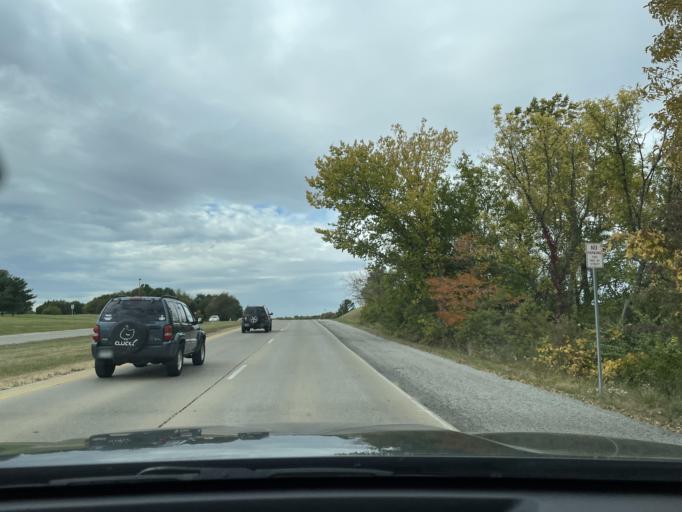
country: US
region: Missouri
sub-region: Buchanan County
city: Saint Joseph
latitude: 39.7698
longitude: -94.8080
